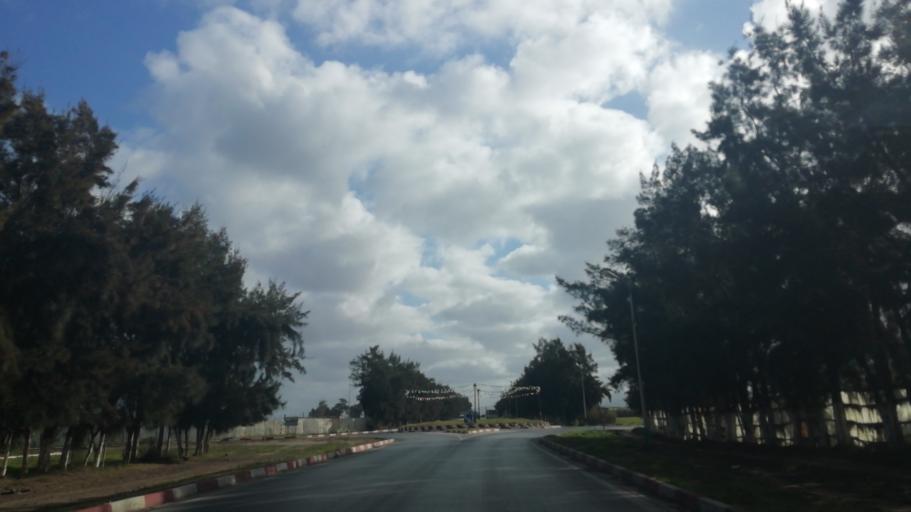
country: DZ
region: Relizane
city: Mazouna
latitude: 36.2554
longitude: 0.5819
